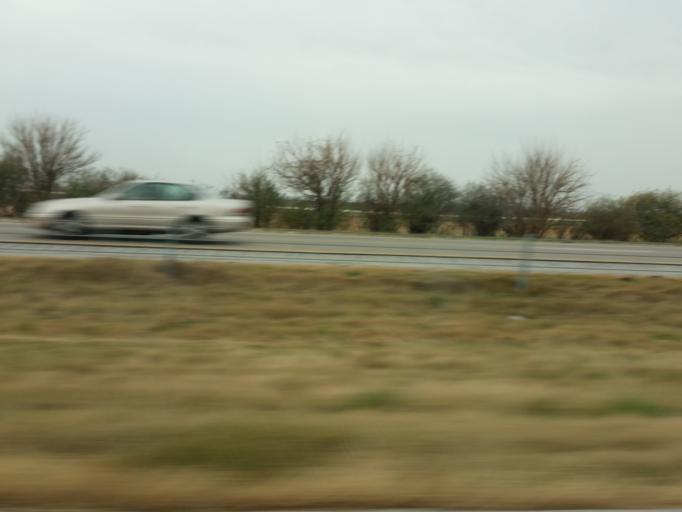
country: US
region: Iowa
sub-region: Scott County
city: Walcott
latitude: 41.6255
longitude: -90.8150
